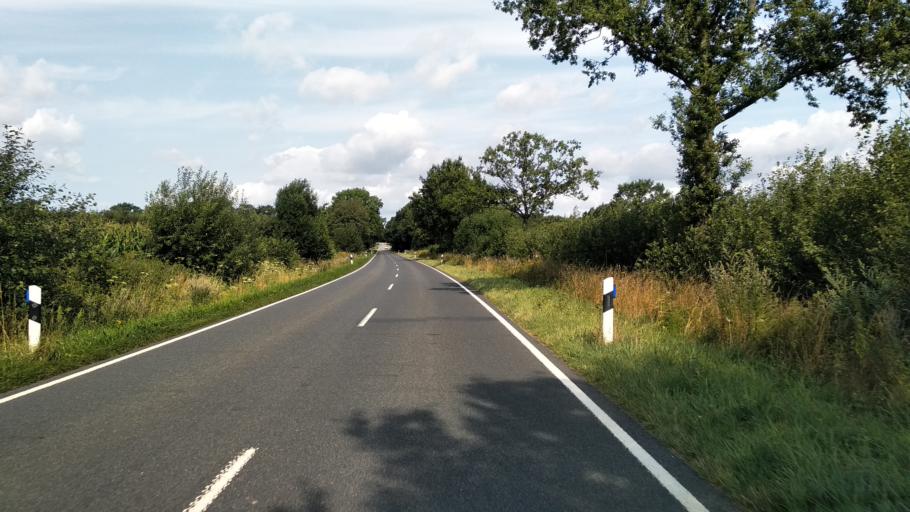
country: DE
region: Schleswig-Holstein
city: Selk
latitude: 54.4641
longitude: 9.5789
